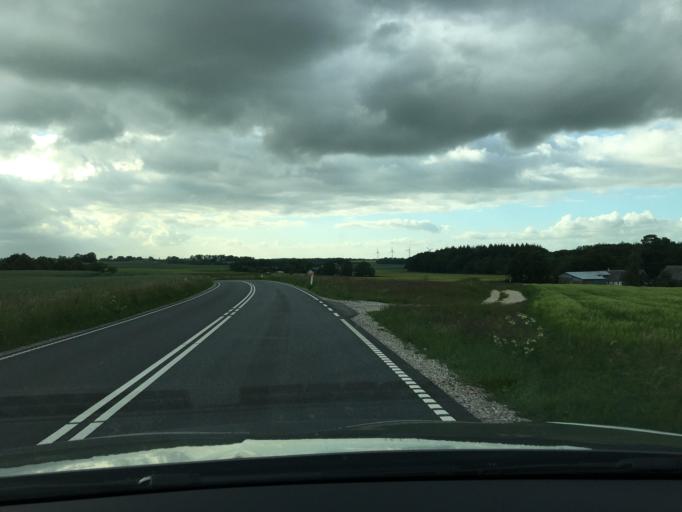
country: DK
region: Central Jutland
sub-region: Arhus Kommune
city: Logten
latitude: 56.2991
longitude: 10.2772
